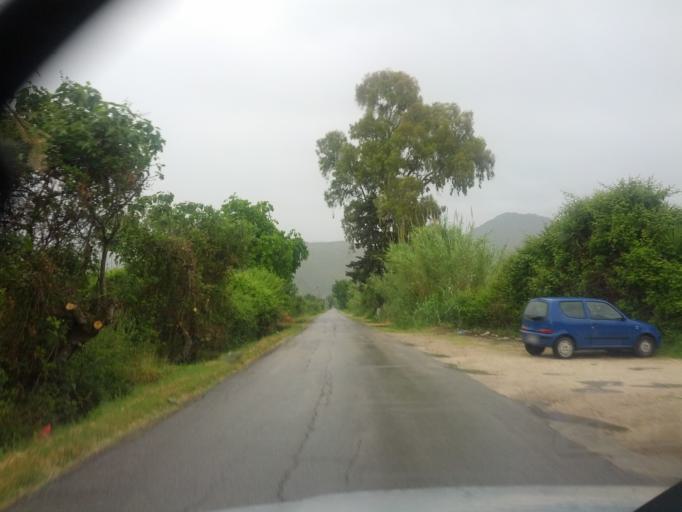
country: IT
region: Latium
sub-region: Provincia di Latina
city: Fondi
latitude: 41.3395
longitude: 13.4291
